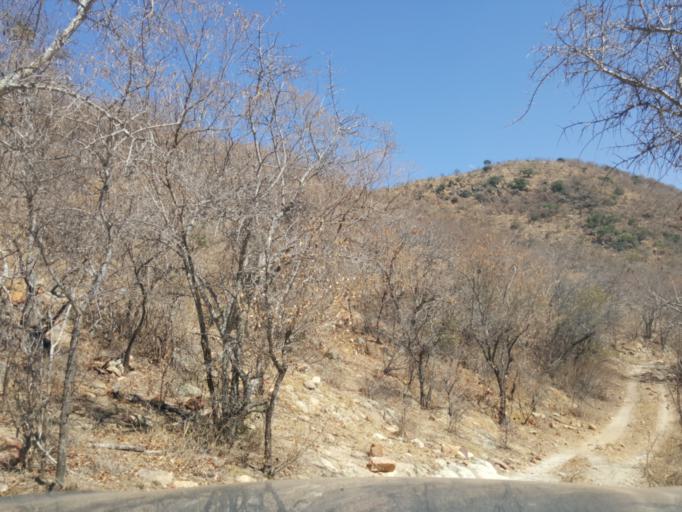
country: BW
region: South East
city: Lobatse
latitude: -25.1554
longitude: 25.6732
